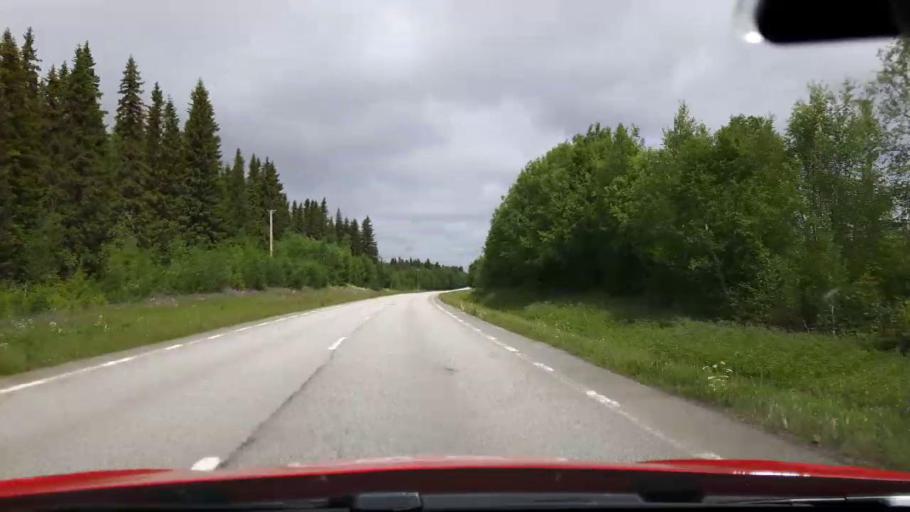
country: SE
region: Jaemtland
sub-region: Krokoms Kommun
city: Krokom
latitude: 63.4946
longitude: 14.5080
